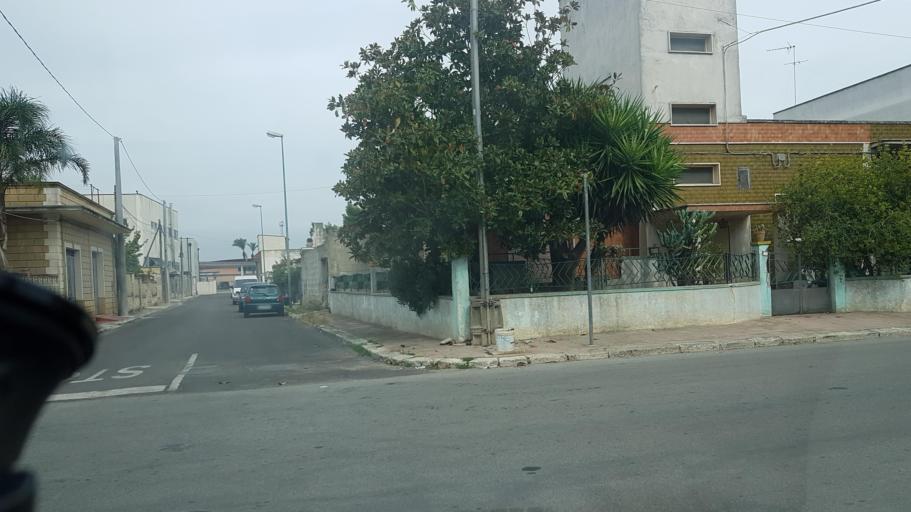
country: IT
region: Apulia
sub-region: Provincia di Brindisi
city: Cellino San Marco
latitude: 40.4756
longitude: 17.9643
